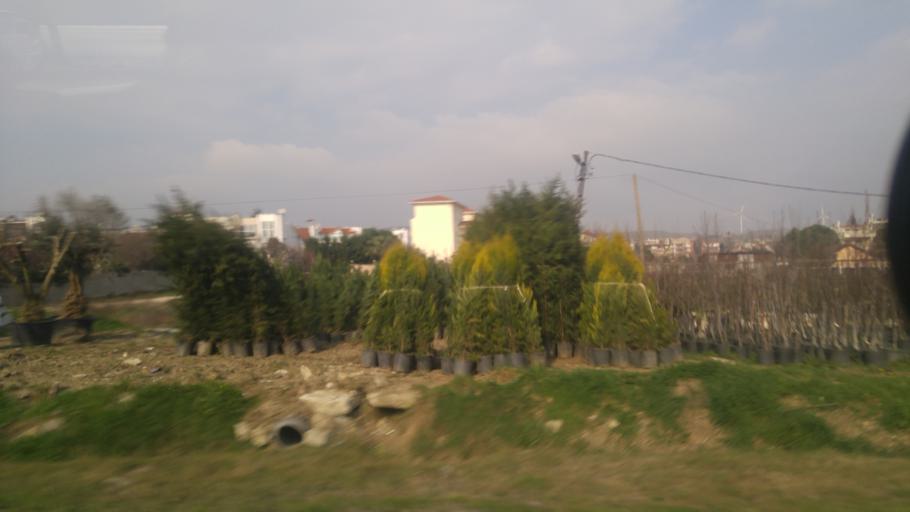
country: TR
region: Istanbul
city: Celaliye
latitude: 41.0414
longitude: 28.4234
